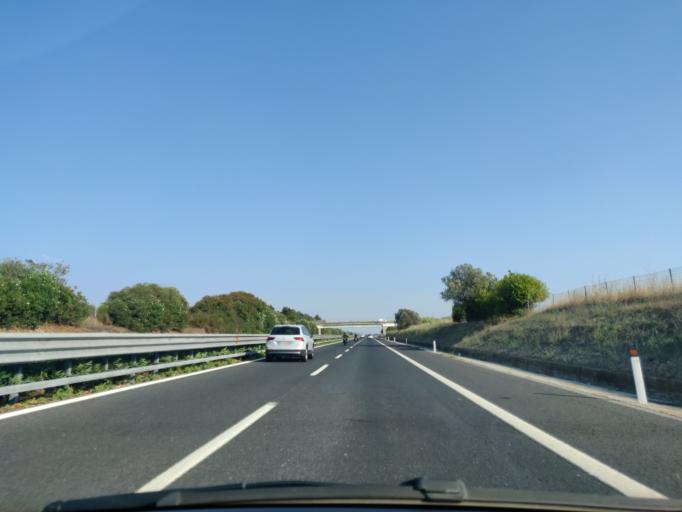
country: IT
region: Latium
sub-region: Citta metropolitana di Roma Capitale
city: Cerveteri
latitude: 41.9742
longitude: 12.0967
